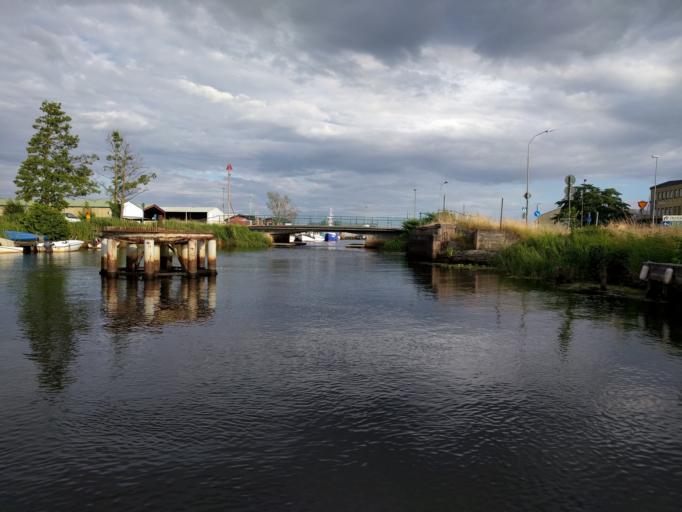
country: SE
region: Blekinge
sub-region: Ronneby Kommun
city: Ronneby
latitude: 56.1774
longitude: 15.2997
